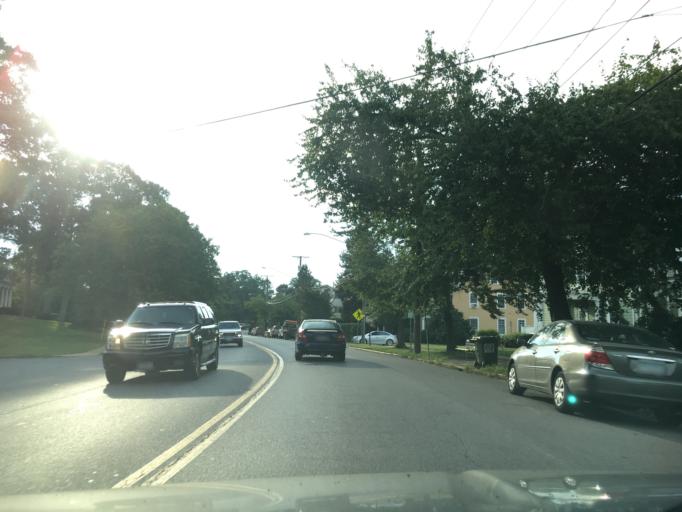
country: US
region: Virginia
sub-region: City of Lynchburg
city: West Lynchburg
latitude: 37.4373
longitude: -79.1744
